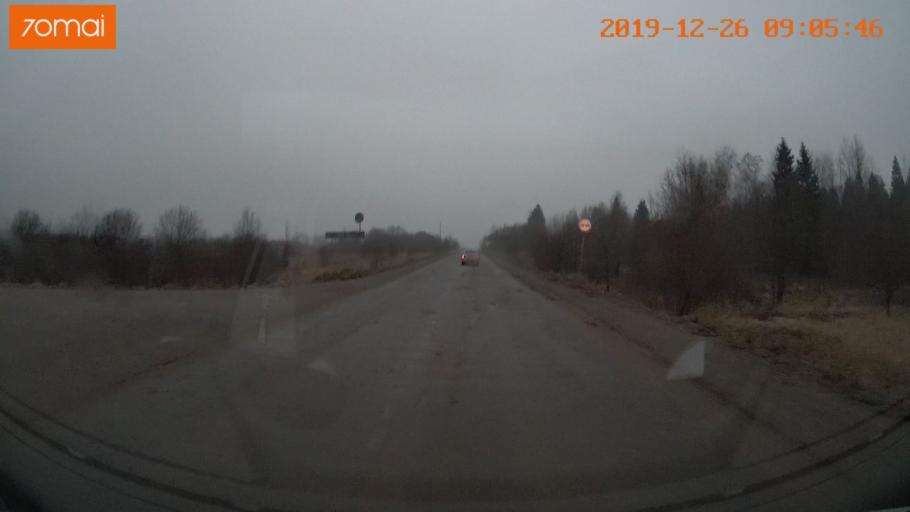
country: RU
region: Vologda
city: Gryazovets
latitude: 58.8291
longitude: 40.2566
